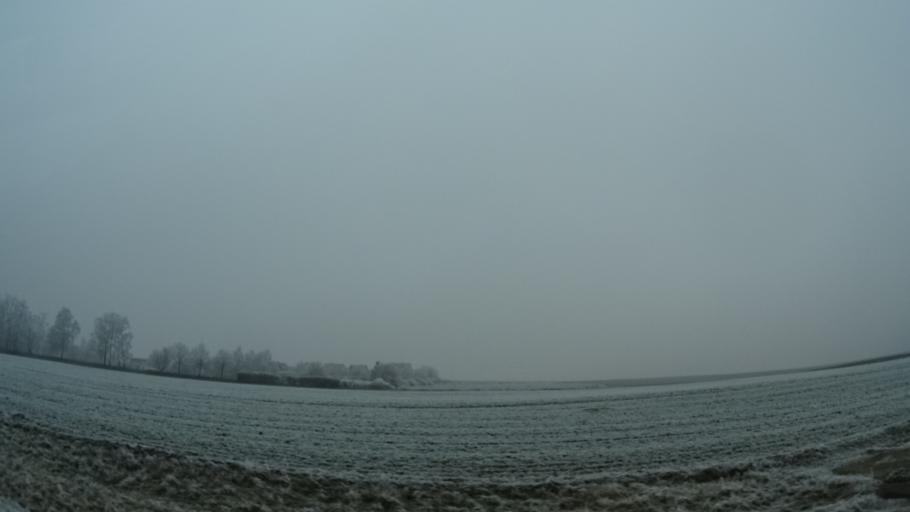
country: DE
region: Bavaria
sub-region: Regierungsbezirk Unterfranken
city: Hassfurt
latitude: 50.0583
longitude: 10.5294
